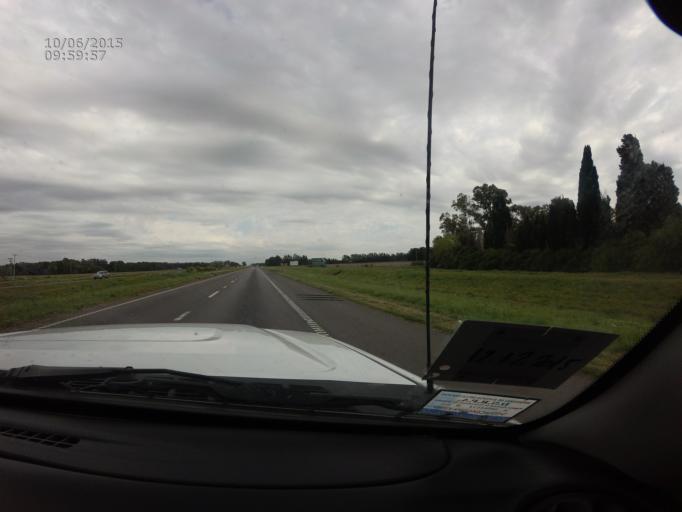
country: AR
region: Buenos Aires
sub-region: Partido de Baradero
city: Baradero
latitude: -33.8999
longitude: -59.4711
